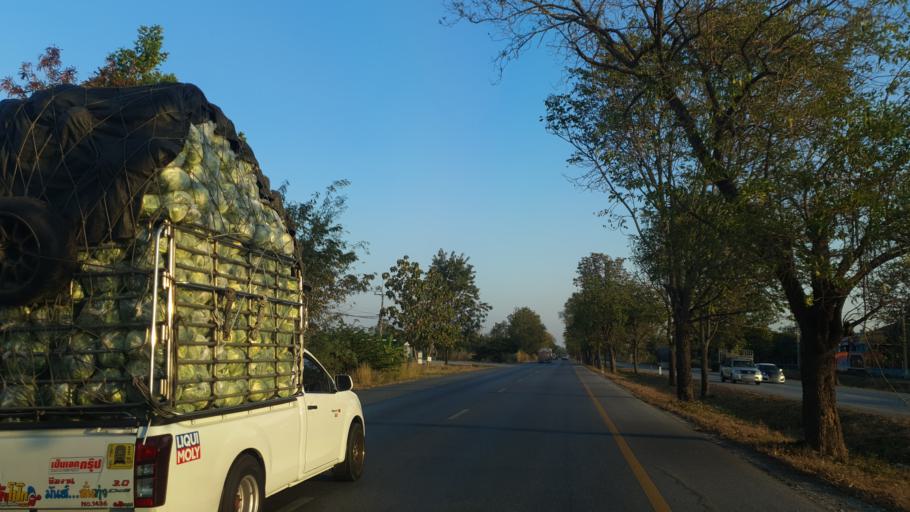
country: TH
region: Kamphaeng Phet
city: Khanu Woralaksaburi
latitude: 16.0217
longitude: 99.7819
